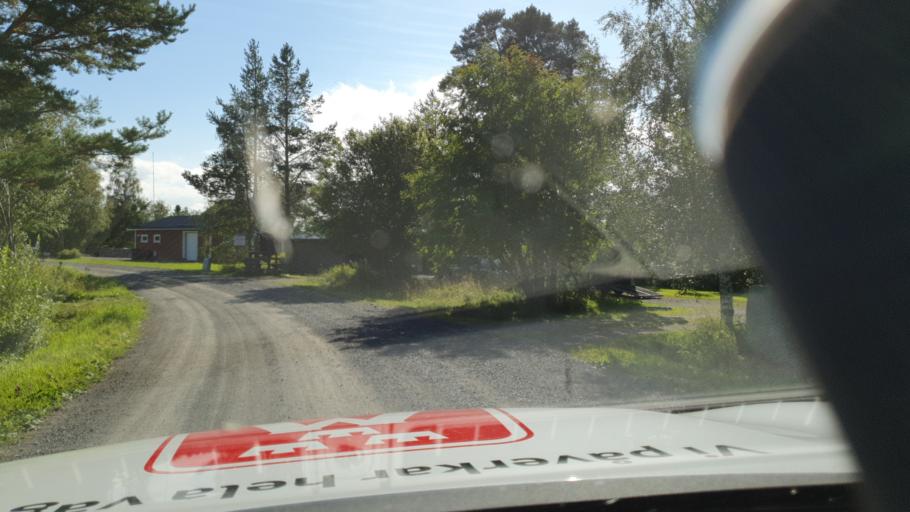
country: SE
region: Jaemtland
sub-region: OEstersunds Kommun
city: Ostersund
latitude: 63.0570
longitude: 14.4412
